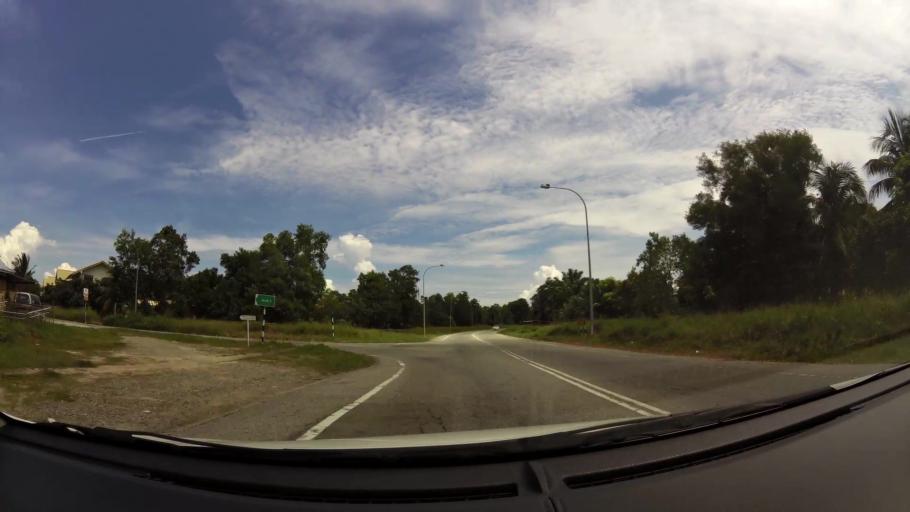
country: BN
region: Brunei and Muara
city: Bandar Seri Begawan
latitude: 4.9571
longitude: 114.9040
